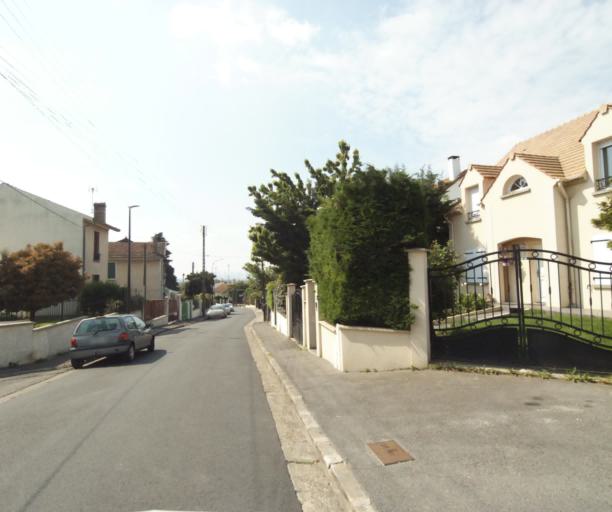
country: FR
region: Ile-de-France
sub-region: Departement du Val-d'Oise
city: Sannois
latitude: 48.9585
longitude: 2.2447
